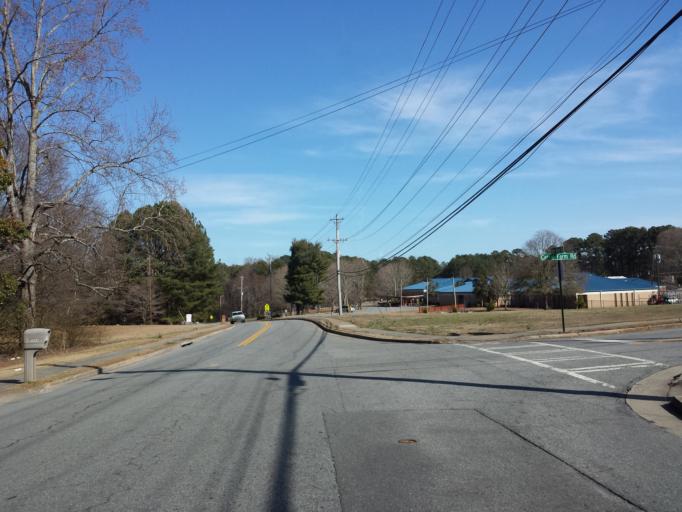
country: US
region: Georgia
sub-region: Cobb County
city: Kennesaw
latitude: 34.0286
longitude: -84.5990
